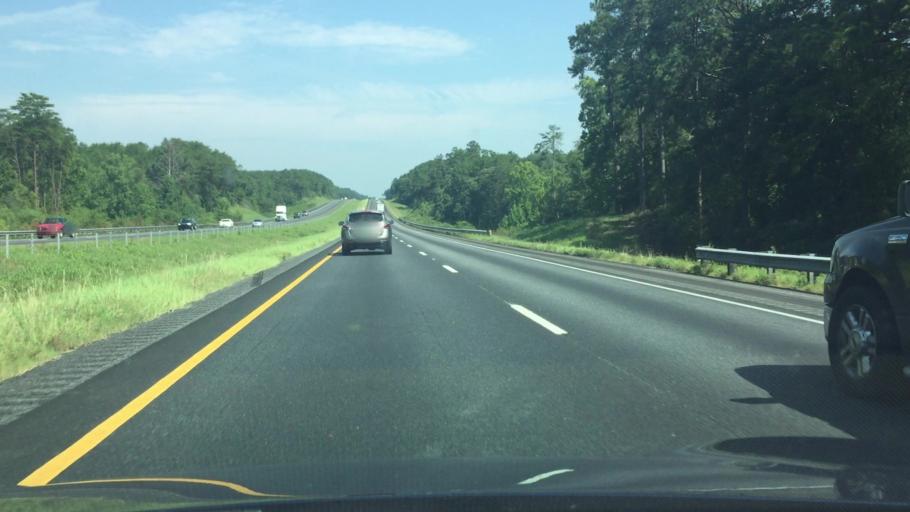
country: US
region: Alabama
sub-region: Chilton County
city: Jemison
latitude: 33.0220
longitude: -86.7164
